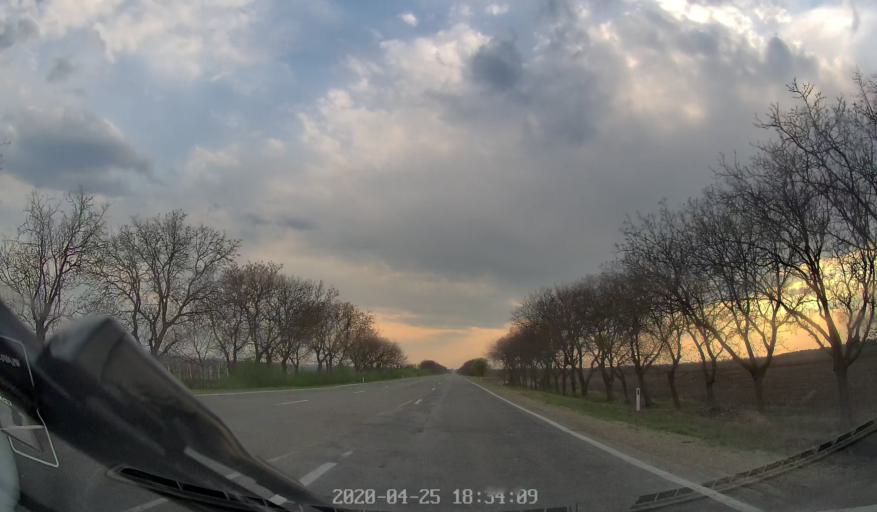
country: MD
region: Criuleni
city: Criuleni
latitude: 47.2184
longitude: 29.1119
